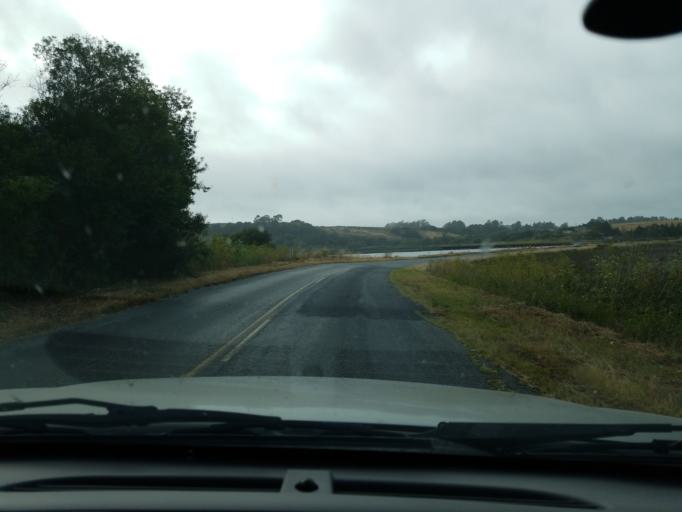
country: US
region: California
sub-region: Monterey County
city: Las Lomas
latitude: 36.8535
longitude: -121.7544
